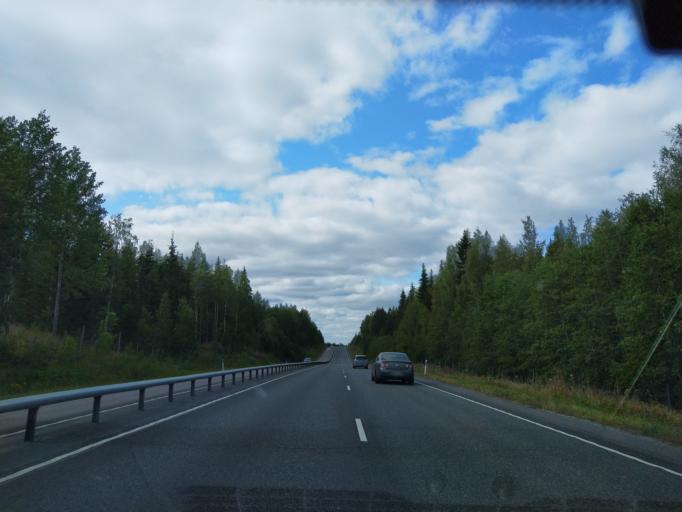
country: FI
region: Haeme
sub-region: Riihimaeki
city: Loppi
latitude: 60.7347
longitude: 24.5523
